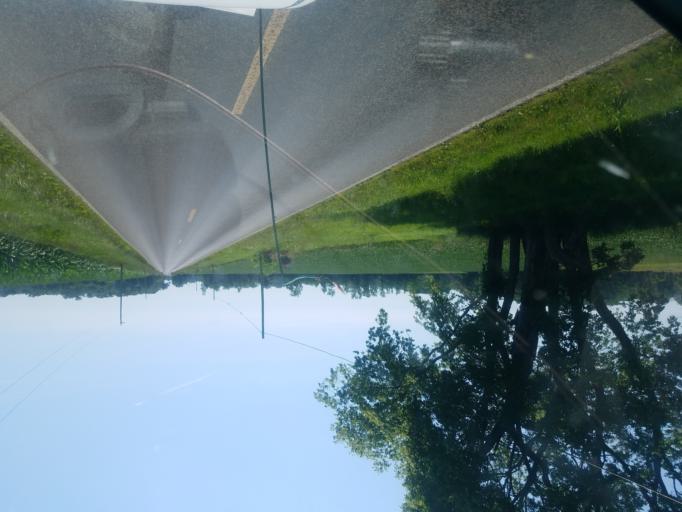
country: US
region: Ohio
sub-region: Champaign County
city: North Lewisburg
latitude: 40.2136
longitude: -83.5042
